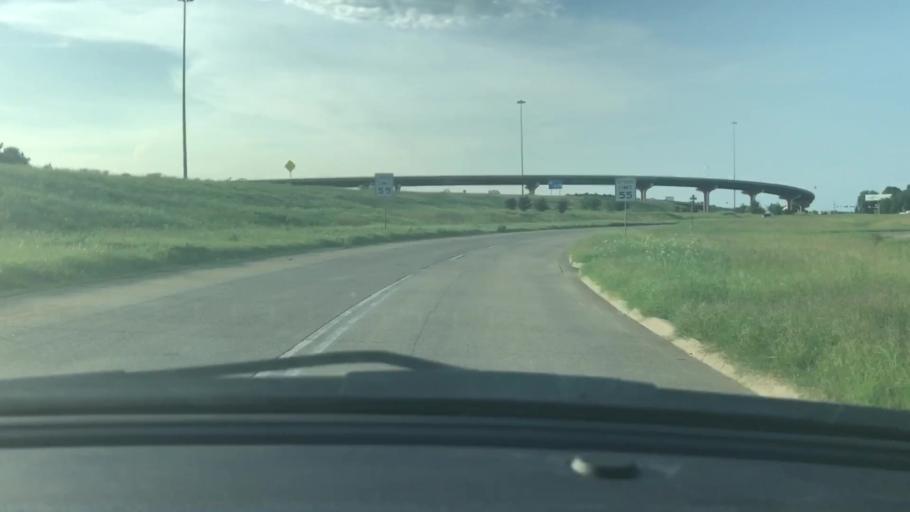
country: US
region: Texas
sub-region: Bowie County
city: Wake Village
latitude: 33.3909
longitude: -94.0969
